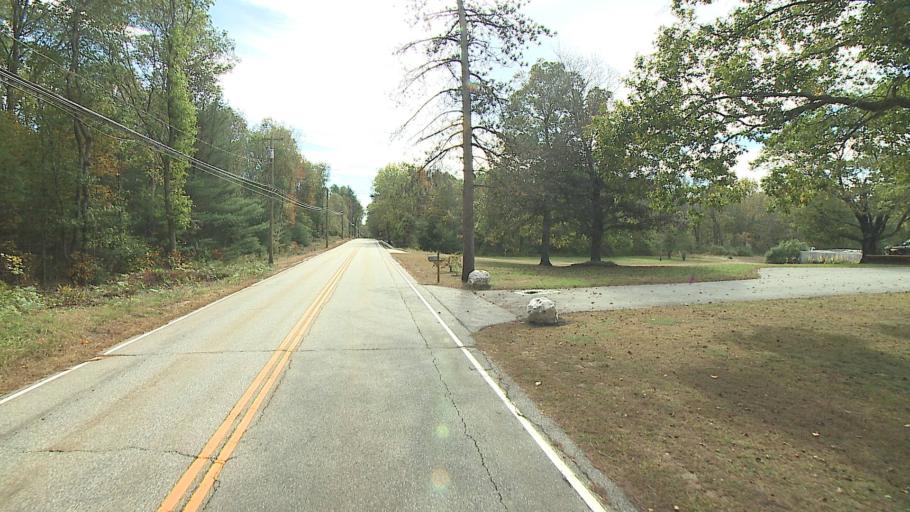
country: US
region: Connecticut
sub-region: Windham County
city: Killingly Center
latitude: 41.8811
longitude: -71.8750
